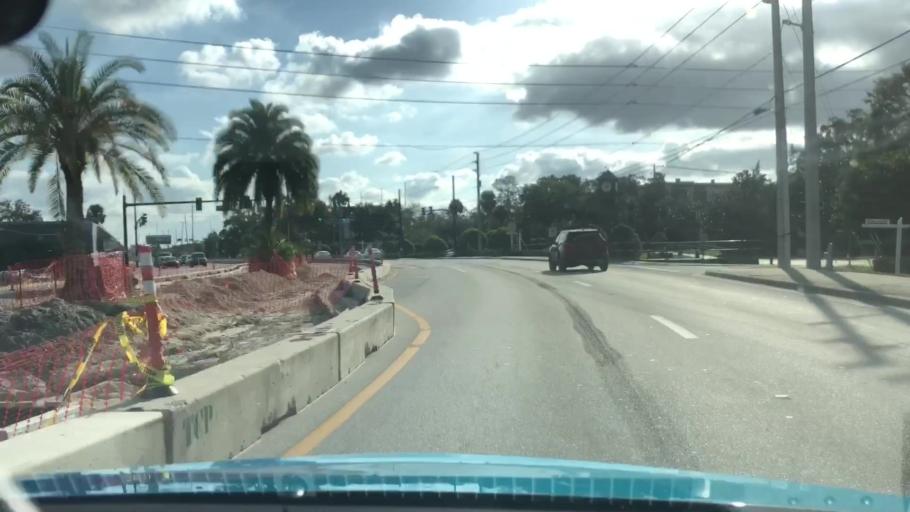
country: US
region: Florida
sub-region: Seminole County
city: Longwood
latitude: 28.7017
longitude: -81.3464
